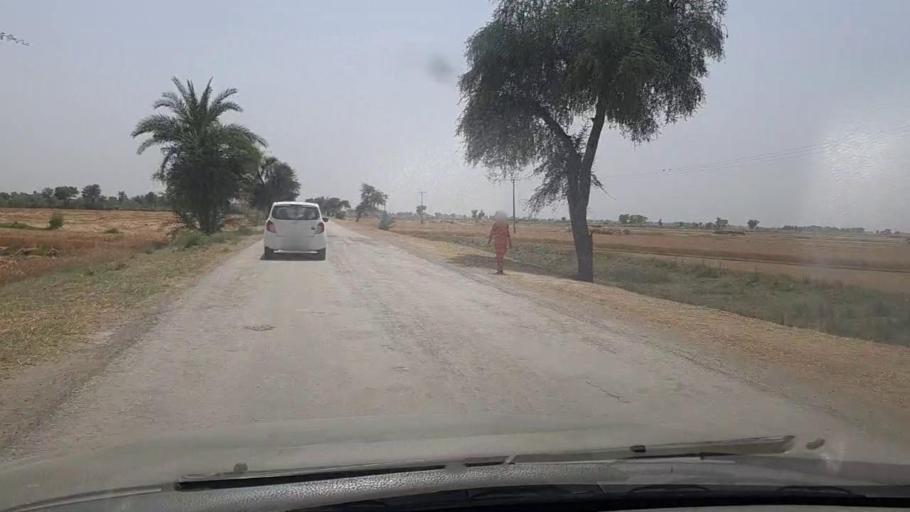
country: PK
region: Sindh
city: Miro Khan
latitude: 27.7209
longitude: 68.0689
